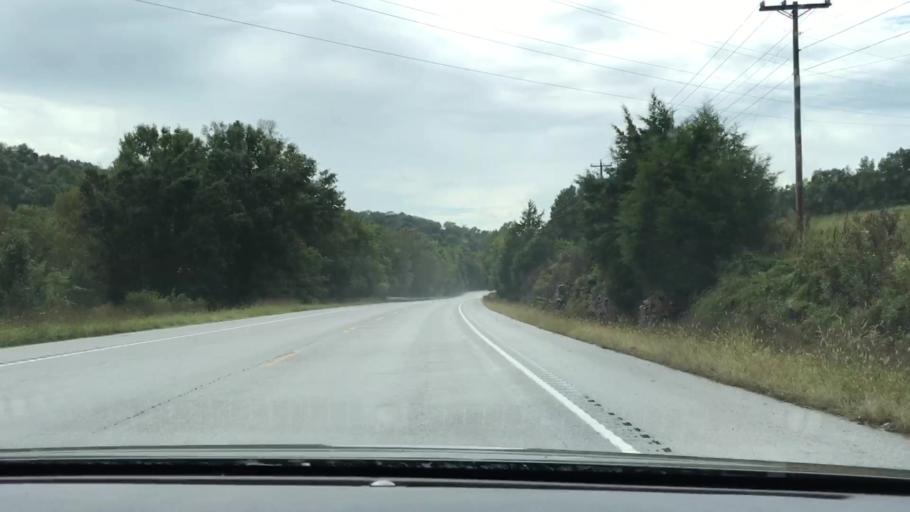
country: US
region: Tennessee
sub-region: Smith County
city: Carthage
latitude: 36.2952
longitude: -85.9825
